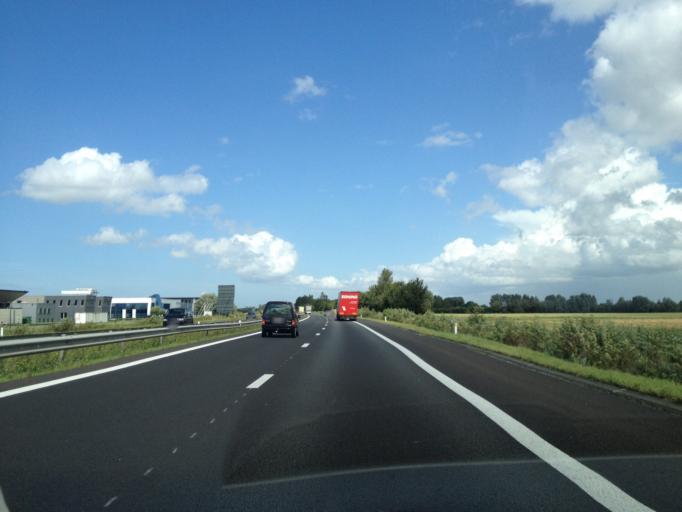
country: BE
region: Flanders
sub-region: Provincie West-Vlaanderen
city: Veurne
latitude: 51.0607
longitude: 2.6823
